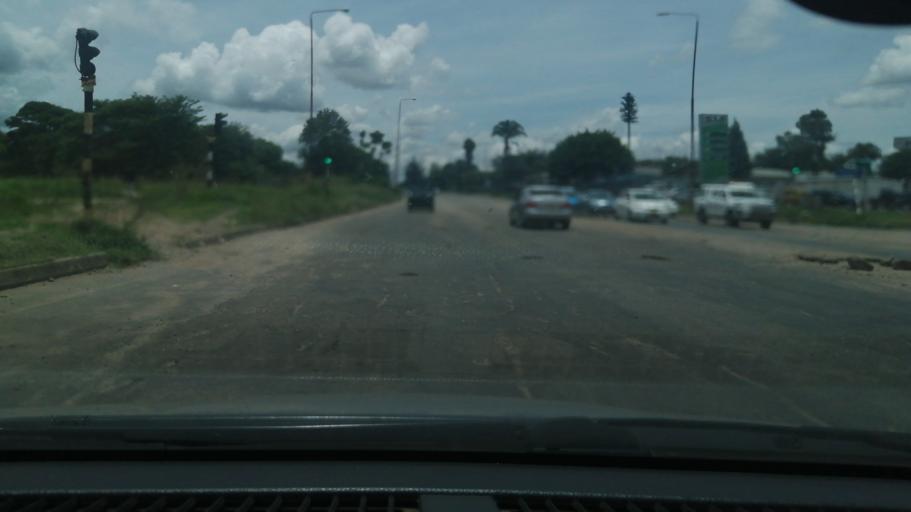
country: ZW
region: Harare
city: Harare
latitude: -17.8815
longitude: 31.0704
